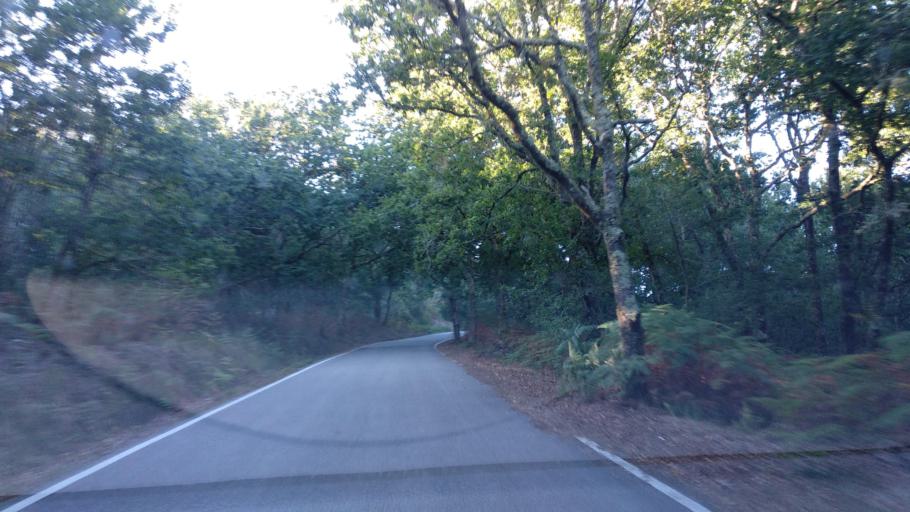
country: ES
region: Galicia
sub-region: Provincia de Pontevedra
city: Fornelos de Montes
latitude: 42.3495
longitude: -8.4891
